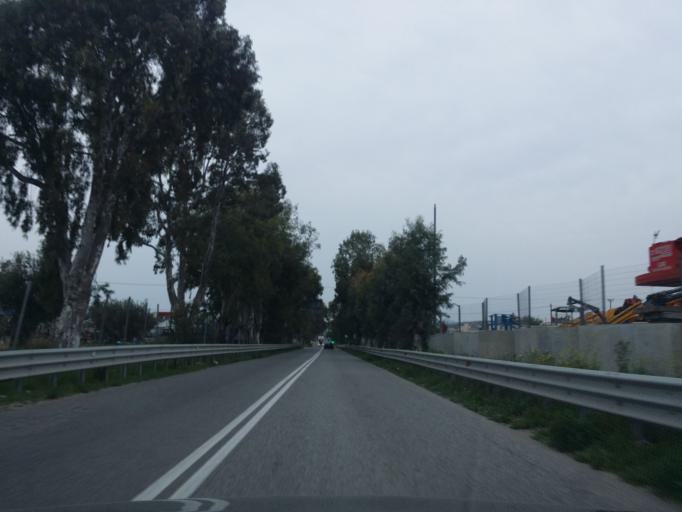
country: GR
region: Attica
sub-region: Nomarchia Dytikis Attikis
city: Mandra
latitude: 38.0828
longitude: 23.4920
